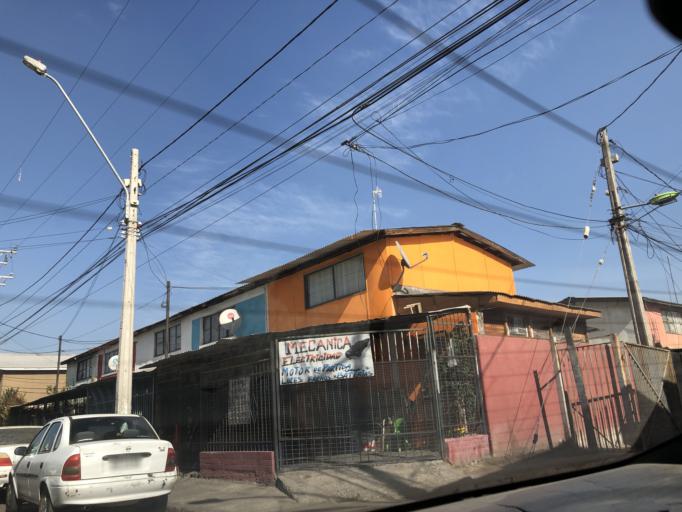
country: CL
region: Santiago Metropolitan
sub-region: Provincia de Santiago
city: La Pintana
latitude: -33.5898
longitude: -70.6024
